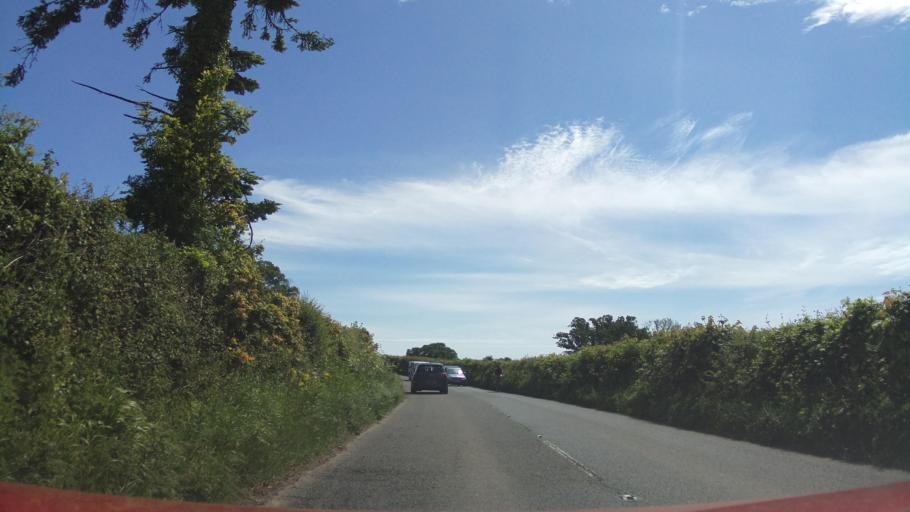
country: GB
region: England
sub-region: Devon
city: Uffculme
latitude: 50.8410
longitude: -3.3145
